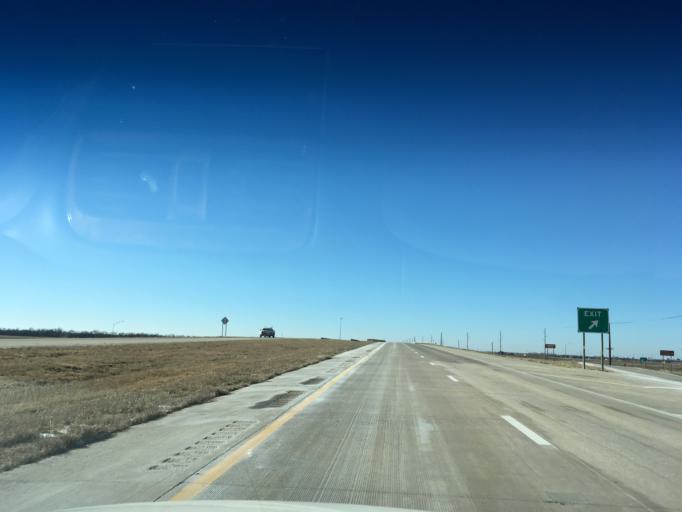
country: US
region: Kansas
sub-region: Reno County
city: Hutchinson
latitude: 38.0288
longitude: -97.8631
